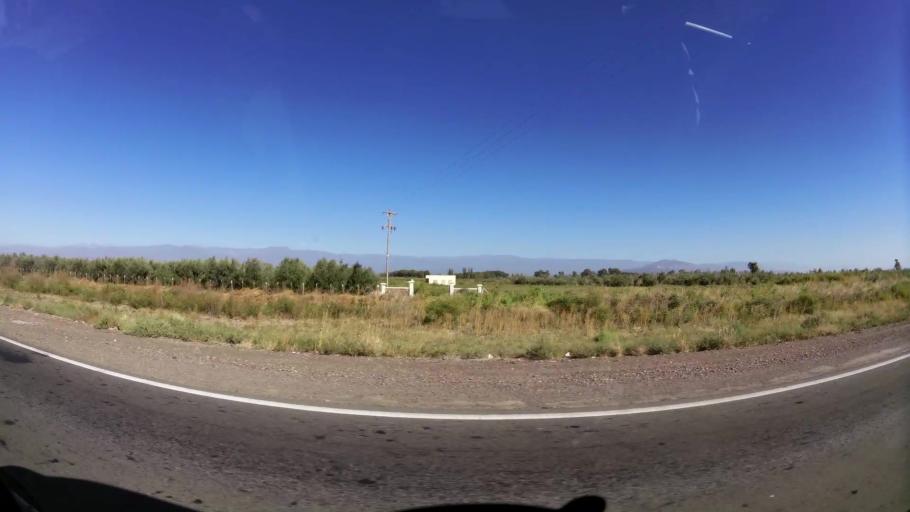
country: AR
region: Mendoza
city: General Lavalle
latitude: -32.7049
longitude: -68.6744
